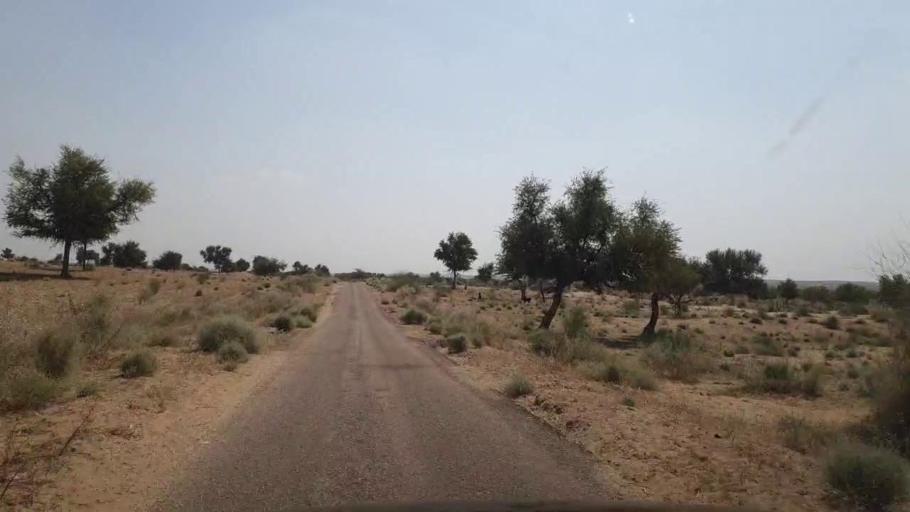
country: PK
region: Sindh
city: Islamkot
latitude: 25.1011
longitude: 70.7401
